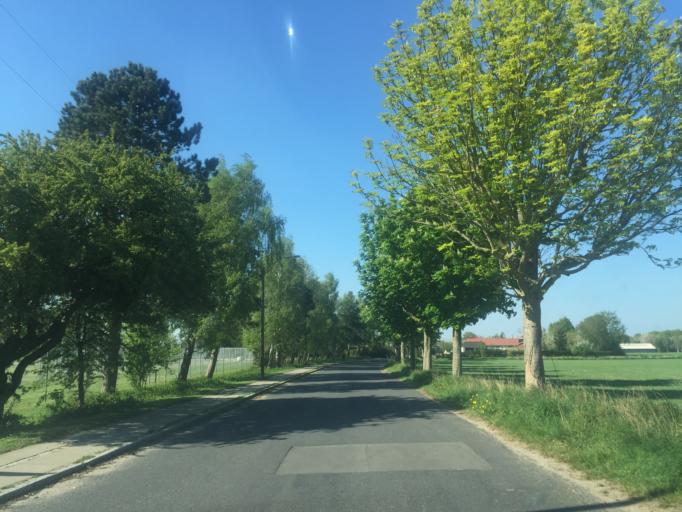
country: DK
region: South Denmark
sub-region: Odense Kommune
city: Hojby
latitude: 55.3593
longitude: 10.4070
